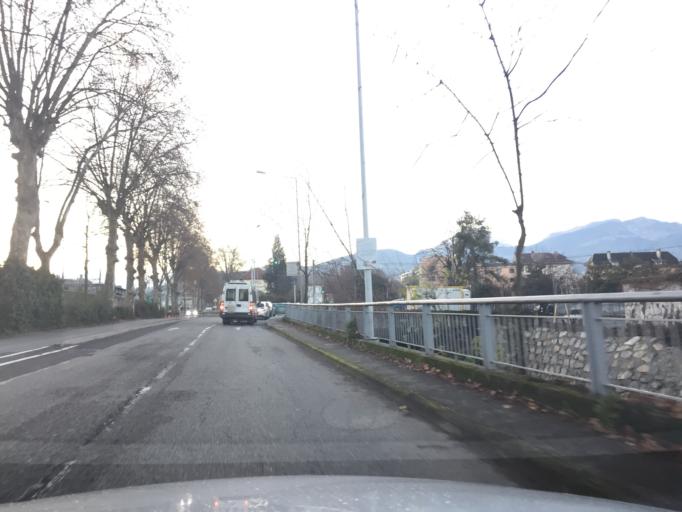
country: FR
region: Rhone-Alpes
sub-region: Departement de la Savoie
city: Chambery
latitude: 45.5778
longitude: 5.9141
